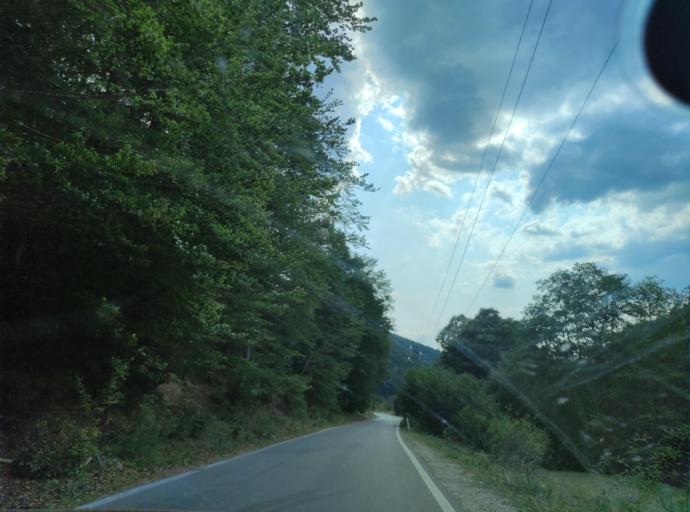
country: BG
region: Blagoevgrad
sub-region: Obshtina Belitsa
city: Belitsa
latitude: 42.0124
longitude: 23.5680
